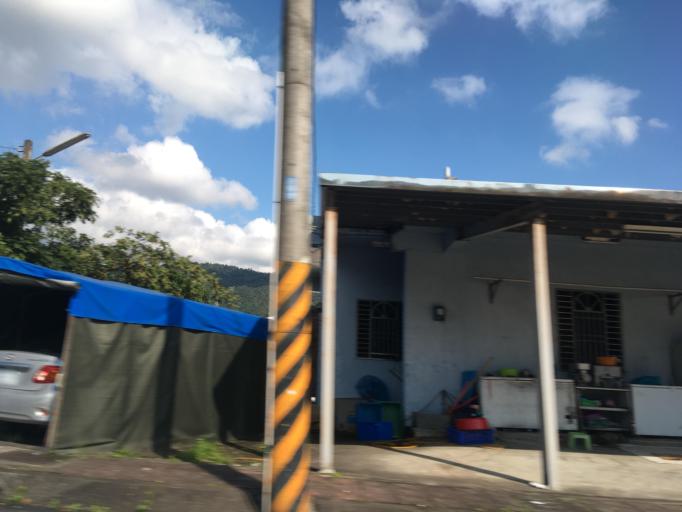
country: TW
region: Taiwan
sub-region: Yilan
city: Yilan
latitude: 24.7458
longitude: 121.6957
